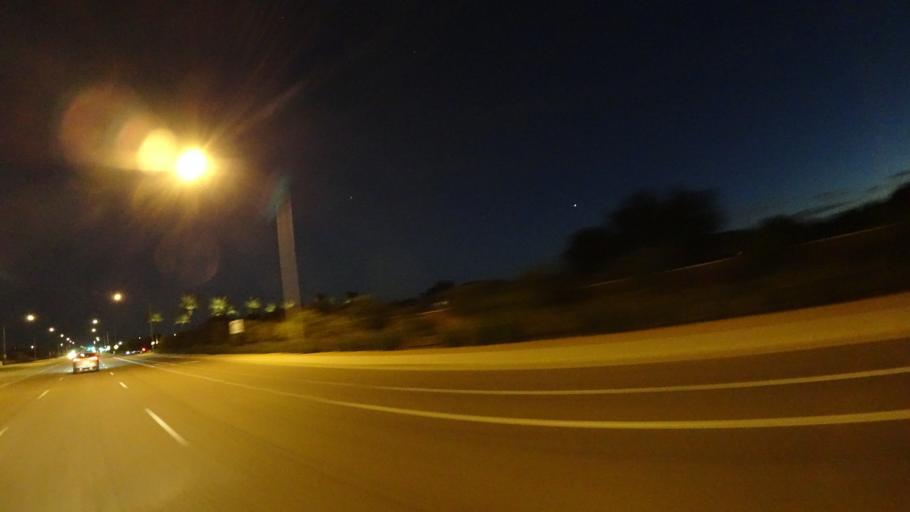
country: US
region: Arizona
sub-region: Maricopa County
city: Mesa
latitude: 33.4518
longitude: -111.7593
